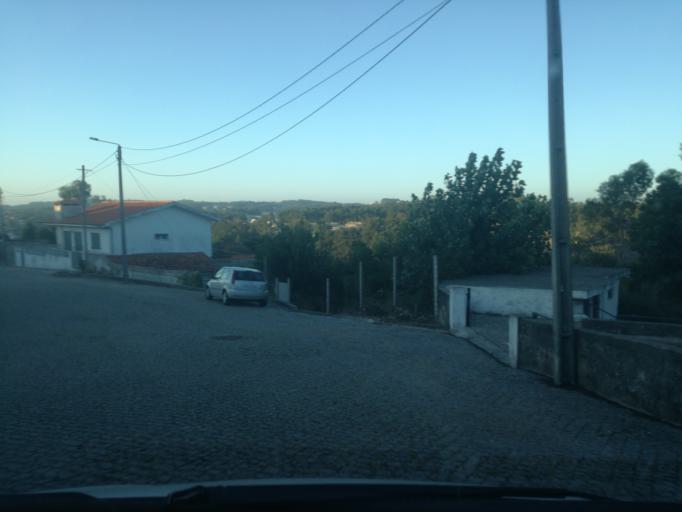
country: PT
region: Porto
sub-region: Maia
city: Nogueira
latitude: 41.2474
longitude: -8.6035
